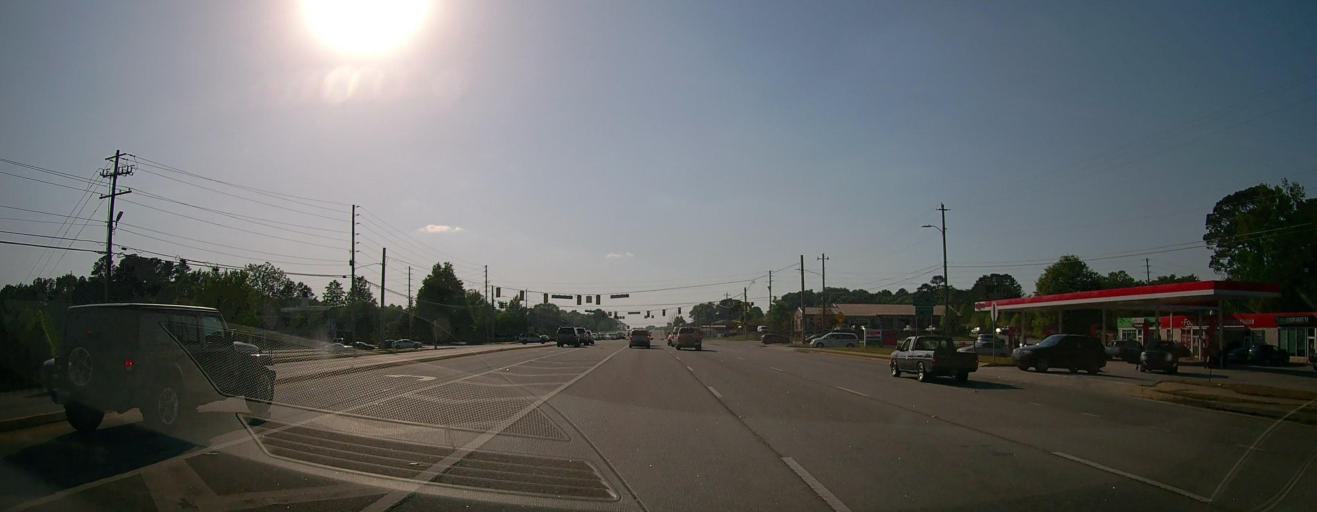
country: US
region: Georgia
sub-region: Newton County
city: Covington
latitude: 33.5990
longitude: -83.8322
